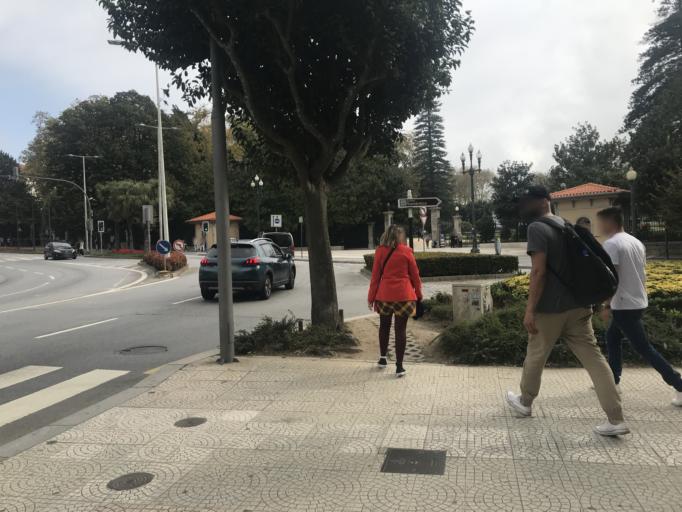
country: PT
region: Porto
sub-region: Porto
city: Porto
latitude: 41.1489
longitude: -8.6257
